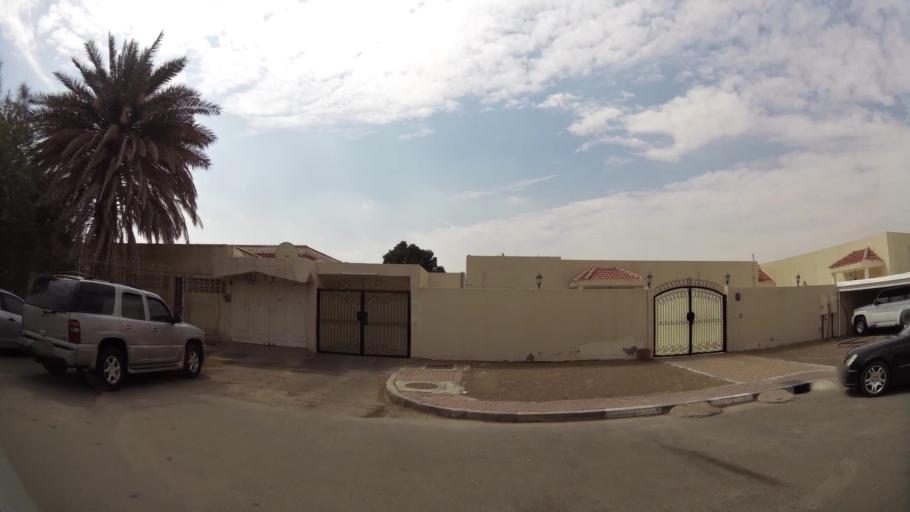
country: AE
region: Abu Dhabi
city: Al Ain
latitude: 24.1981
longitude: 55.7948
